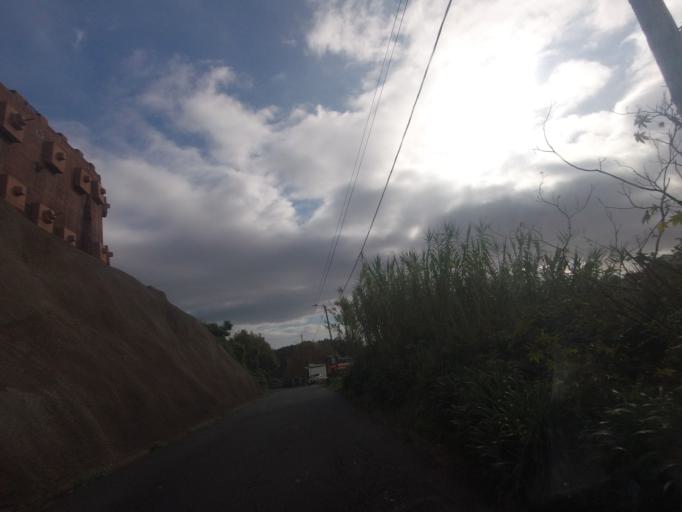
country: PT
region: Madeira
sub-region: Funchal
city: Nossa Senhora do Monte
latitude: 32.6763
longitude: -16.9439
